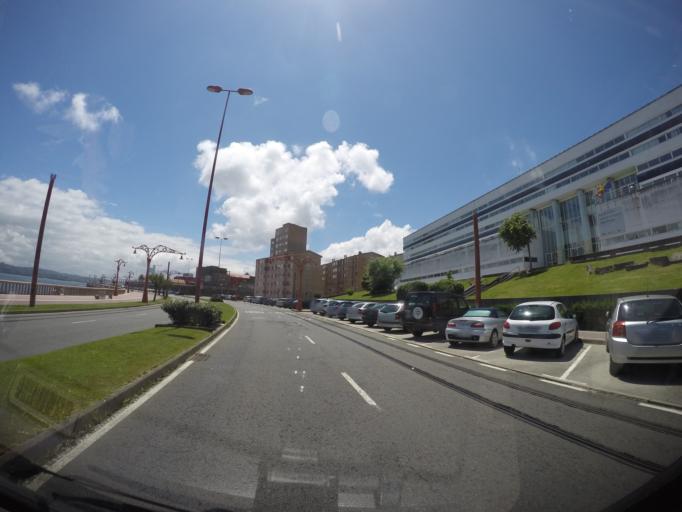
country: ES
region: Galicia
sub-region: Provincia da Coruna
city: A Coruna
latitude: 43.3717
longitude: -8.3899
